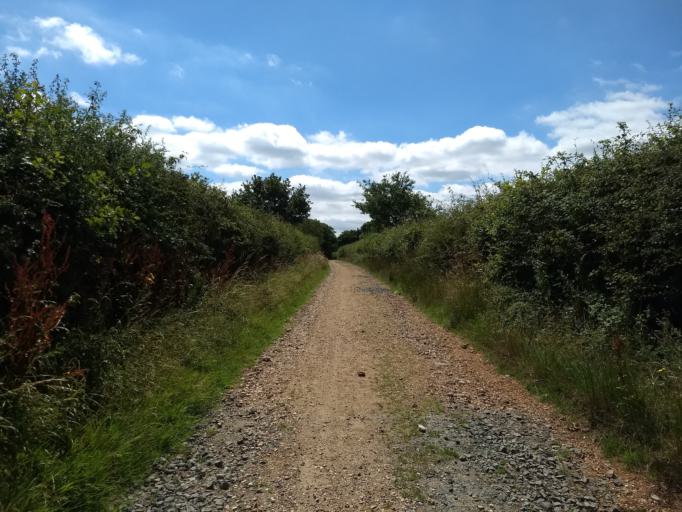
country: GB
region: England
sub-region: Isle of Wight
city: Brading
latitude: 50.7065
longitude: -1.1403
